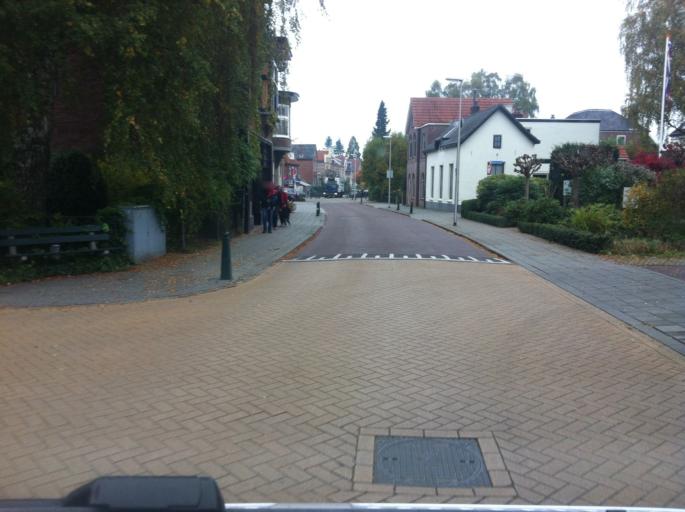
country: NL
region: Gelderland
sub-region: Gemeente Winterswijk
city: Winterswijk
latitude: 51.9732
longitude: 6.7150
